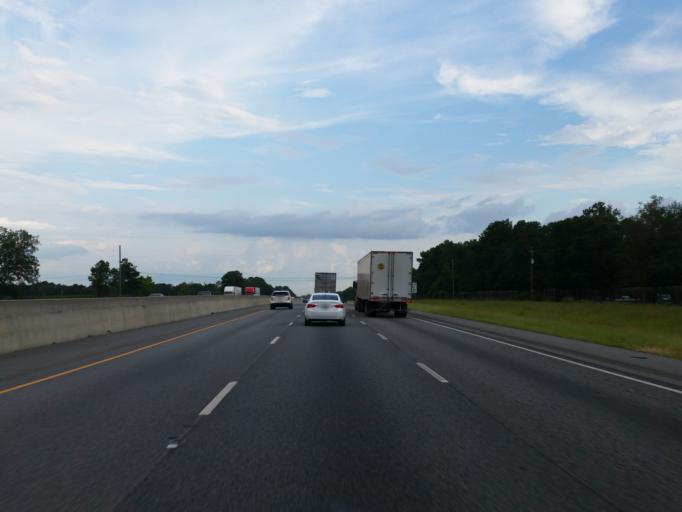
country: US
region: Georgia
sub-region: Lowndes County
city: Hahira
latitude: 31.0169
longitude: -83.3950
